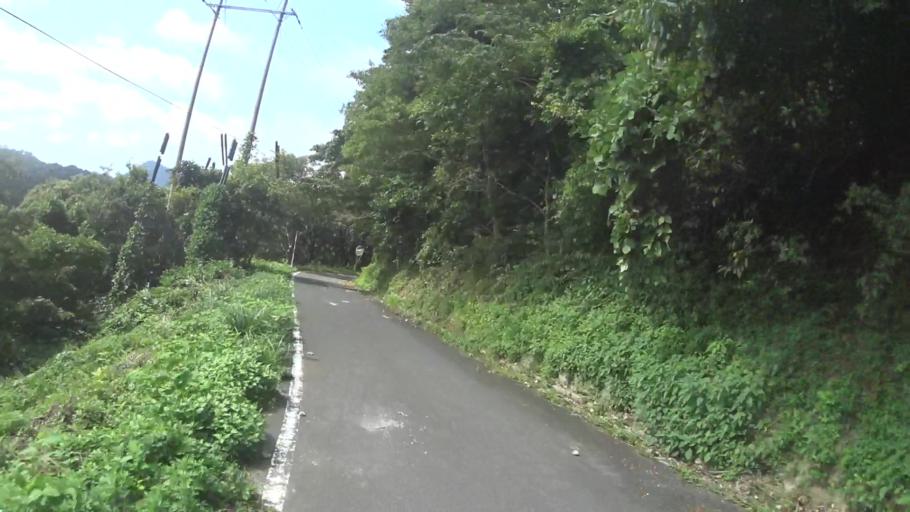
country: JP
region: Kyoto
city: Miyazu
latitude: 35.7315
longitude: 135.1942
